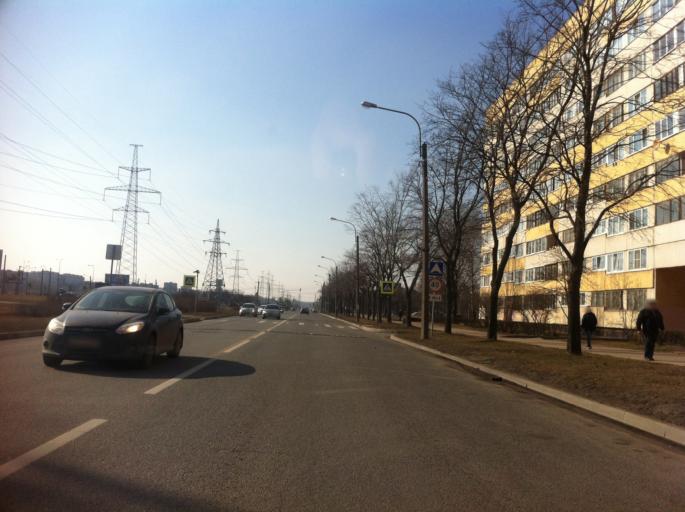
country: RU
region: St.-Petersburg
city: Uritsk
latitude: 59.8472
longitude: 30.1800
